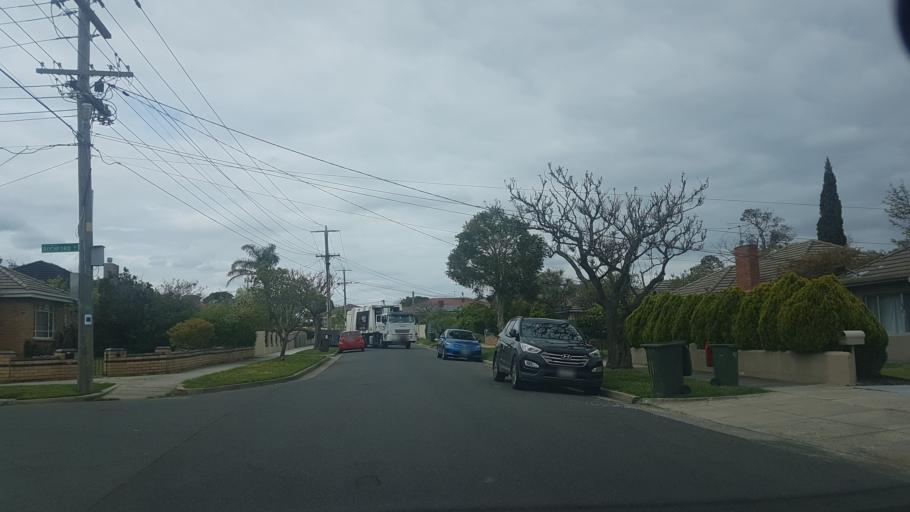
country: AU
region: Victoria
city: McKinnon
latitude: -37.9094
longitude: 145.0575
